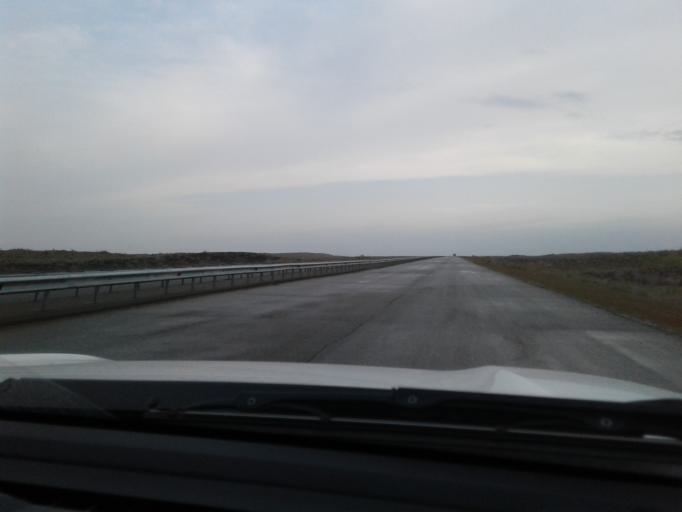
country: TM
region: Ahal
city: Abadan
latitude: 38.4814
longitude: 58.5058
